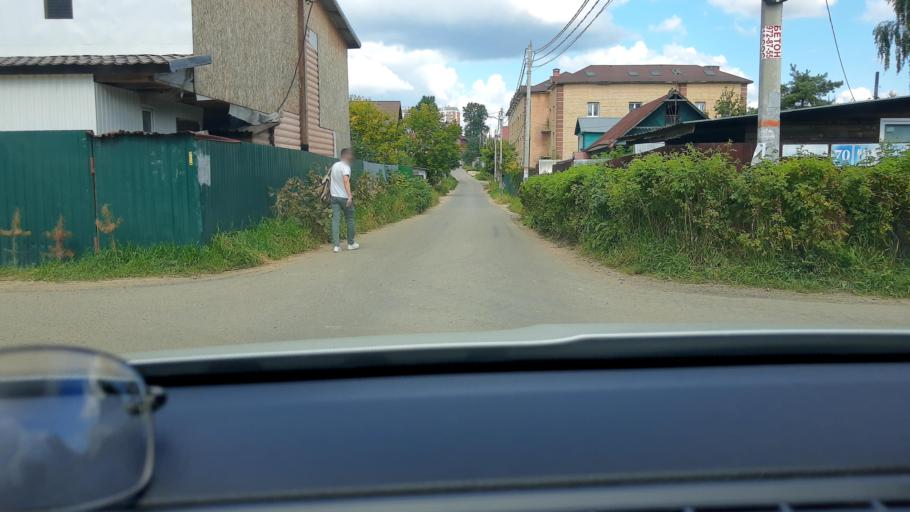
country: RU
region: Moskovskaya
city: Odintsovo
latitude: 55.6846
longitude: 37.3151
